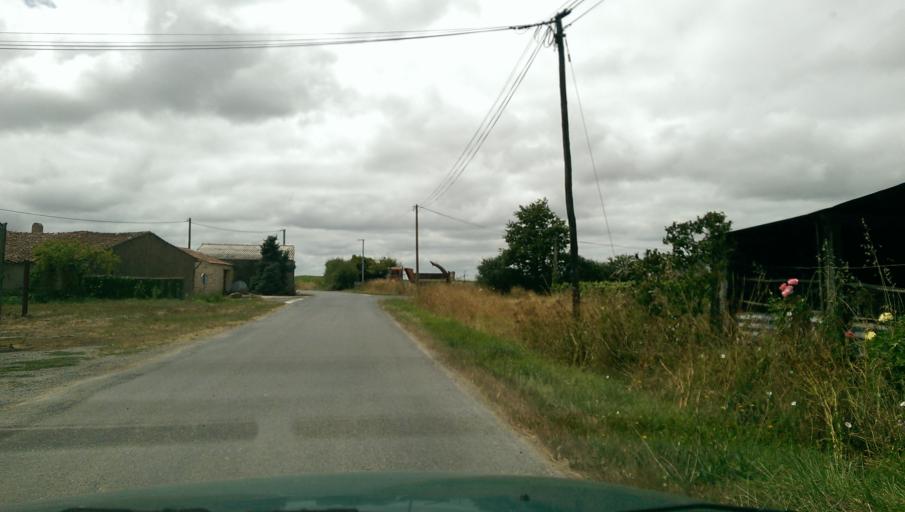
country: FR
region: Pays de la Loire
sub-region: Departement de la Loire-Atlantique
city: Remouille
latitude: 47.0648
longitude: -1.3624
